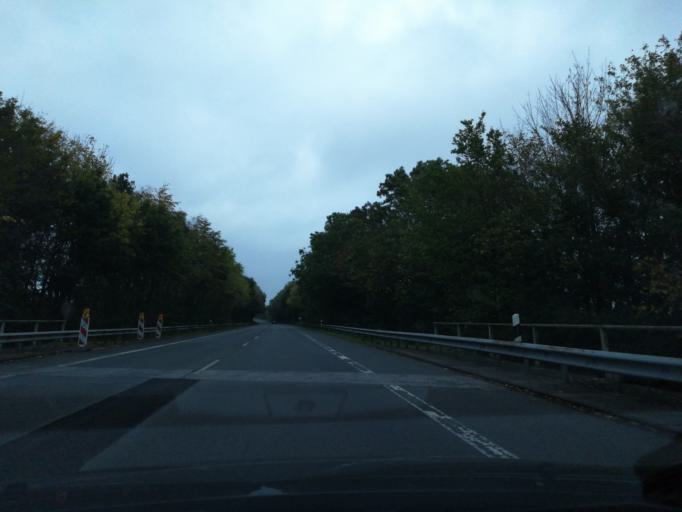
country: DE
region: Lower Saxony
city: Fedderwarden
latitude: 53.5588
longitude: 8.0508
